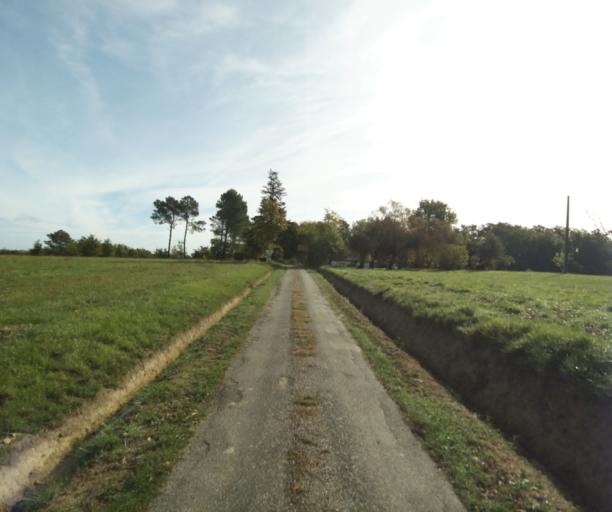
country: FR
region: Midi-Pyrenees
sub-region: Departement du Gers
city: Eauze
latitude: 43.9261
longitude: 0.0918
